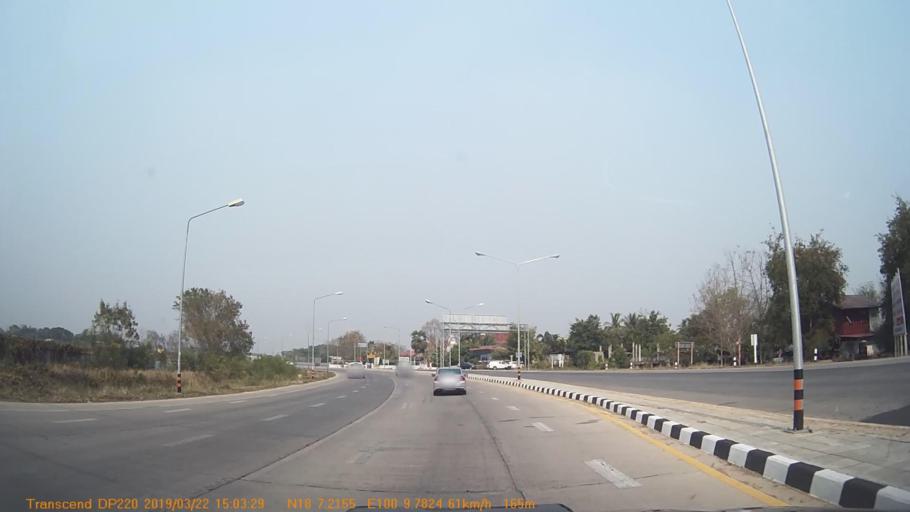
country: TH
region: Phrae
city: Phrae
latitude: 18.1204
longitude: 100.1633
